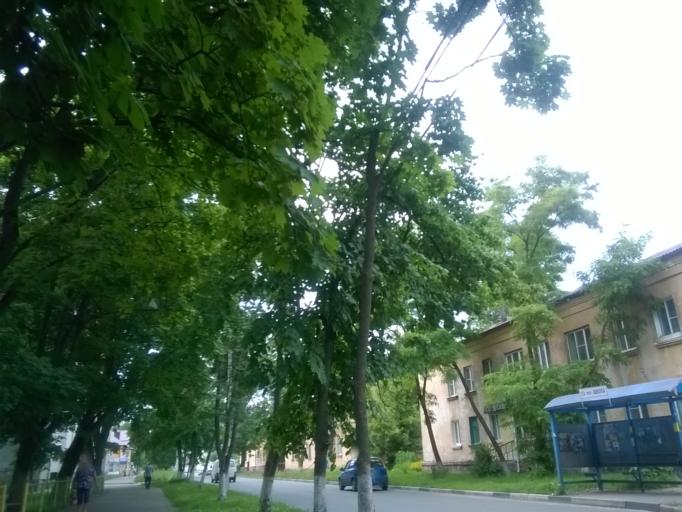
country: RU
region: Kursk
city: Kursk
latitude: 51.6743
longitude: 36.1527
